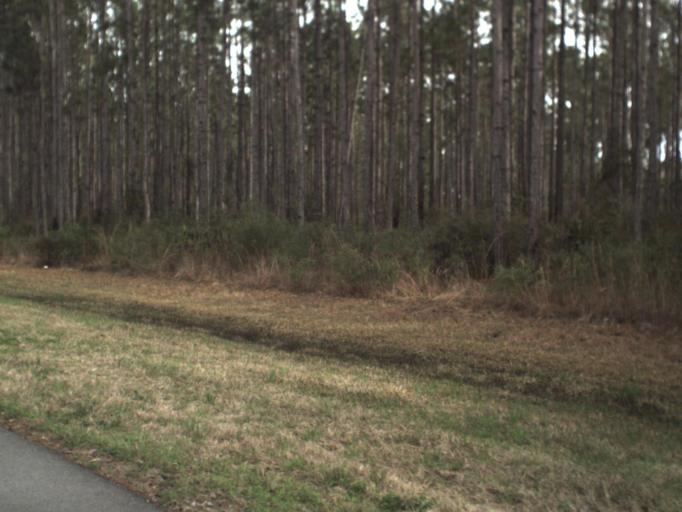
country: US
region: Florida
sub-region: Bay County
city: Callaway
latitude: 30.1451
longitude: -85.4376
